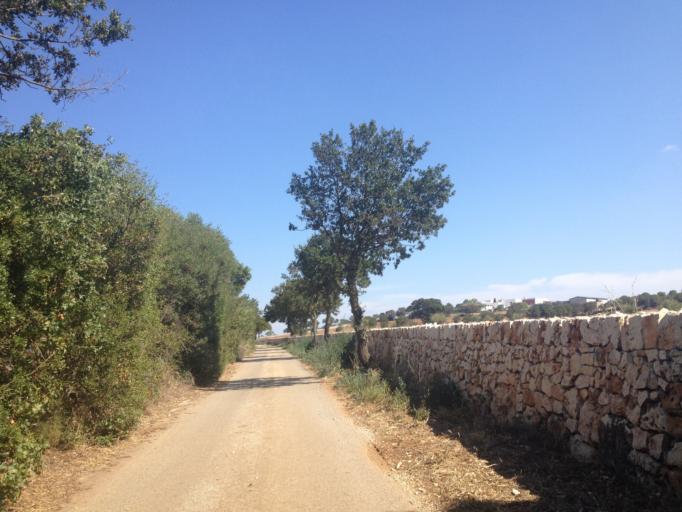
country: IT
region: Apulia
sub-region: Provincia di Bari
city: Sammichele di Bari
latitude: 40.8224
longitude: 17.0145
